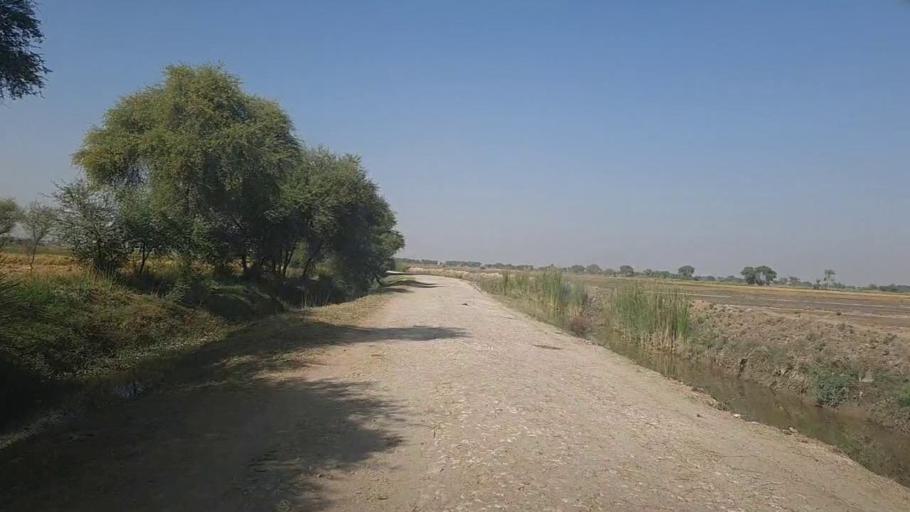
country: PK
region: Sindh
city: Thul
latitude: 28.3055
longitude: 68.7707
